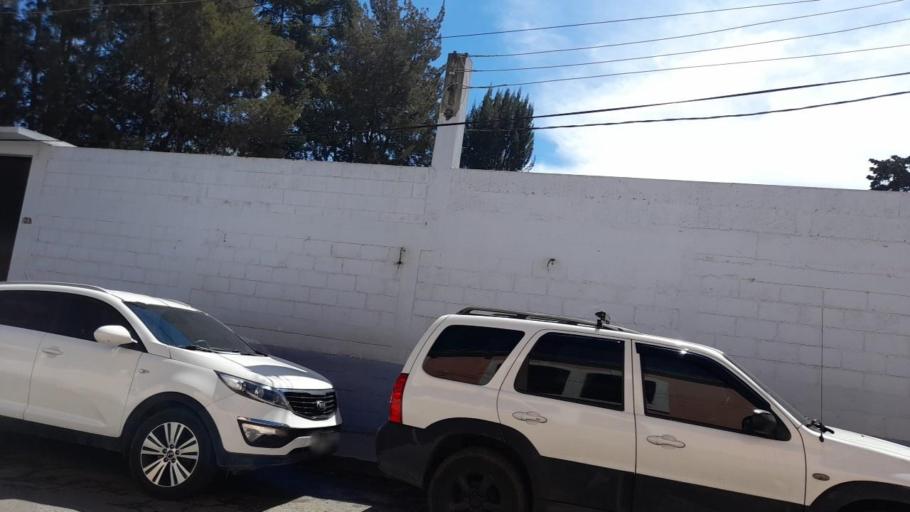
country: GT
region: Quetzaltenango
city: Quetzaltenango
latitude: 14.8399
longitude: -91.5187
